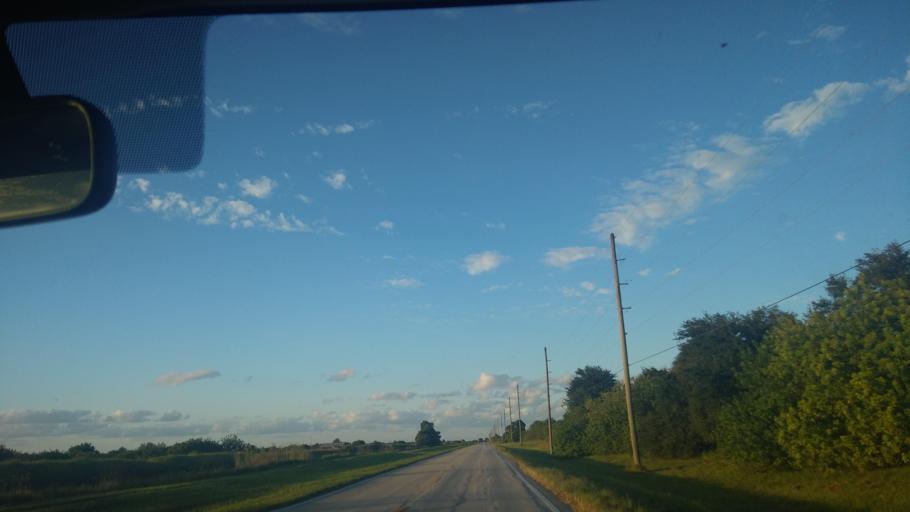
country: US
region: Florida
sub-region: Indian River County
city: Fellsmere
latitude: 27.7268
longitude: -80.6424
